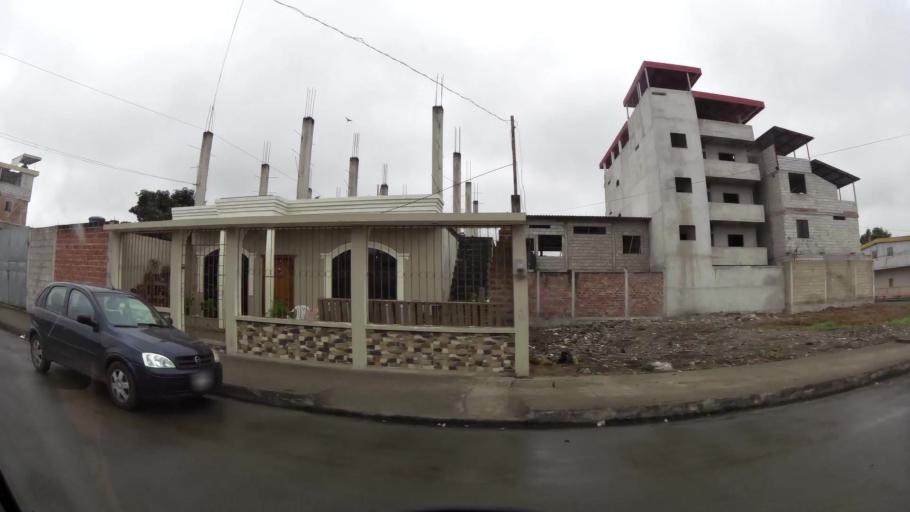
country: EC
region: El Oro
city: Pasaje
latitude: -3.3246
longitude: -79.8159
